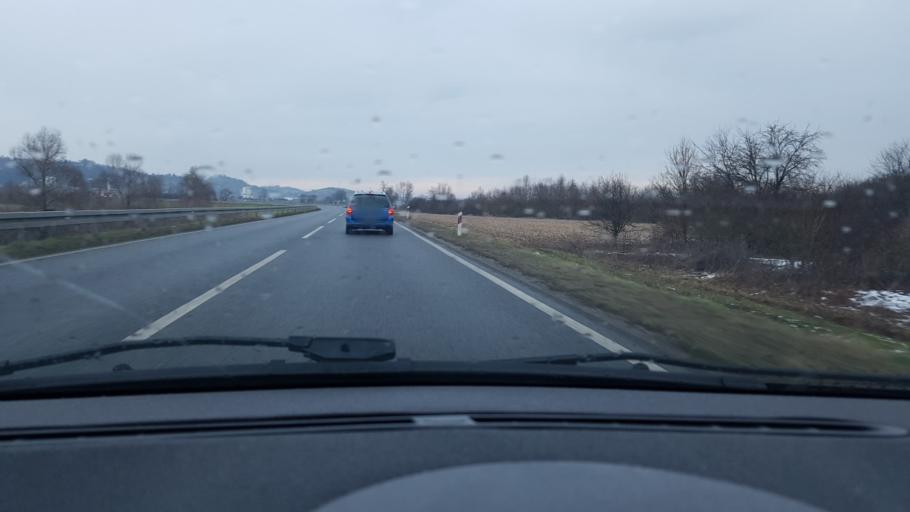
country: HR
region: Zagrebacka
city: Pojatno
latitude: 45.8982
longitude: 15.8160
